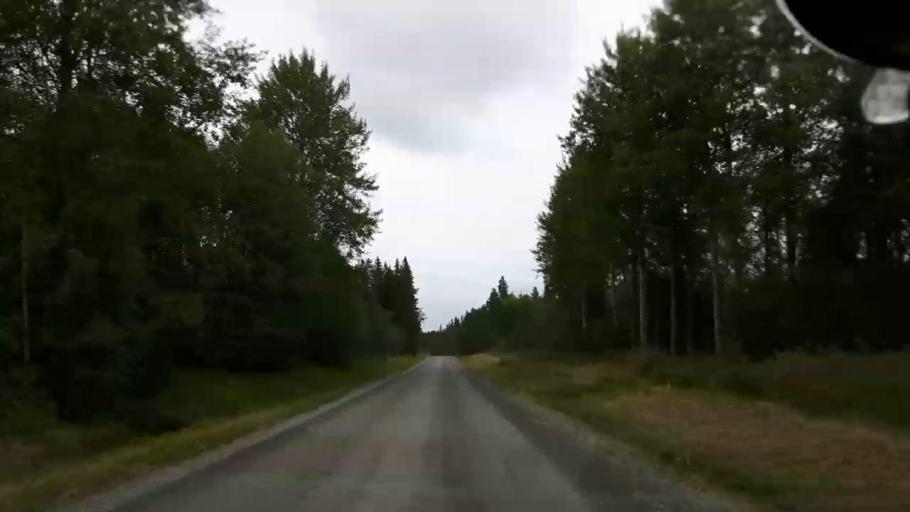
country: SE
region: Jaemtland
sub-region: OEstersunds Kommun
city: Ostersund
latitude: 63.1097
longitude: 14.5455
